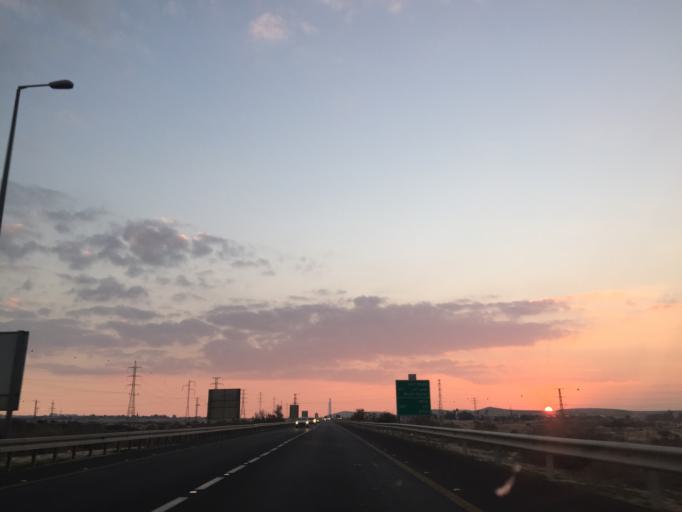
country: IL
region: Southern District
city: Yeroham
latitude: 31.0091
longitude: 34.7792
